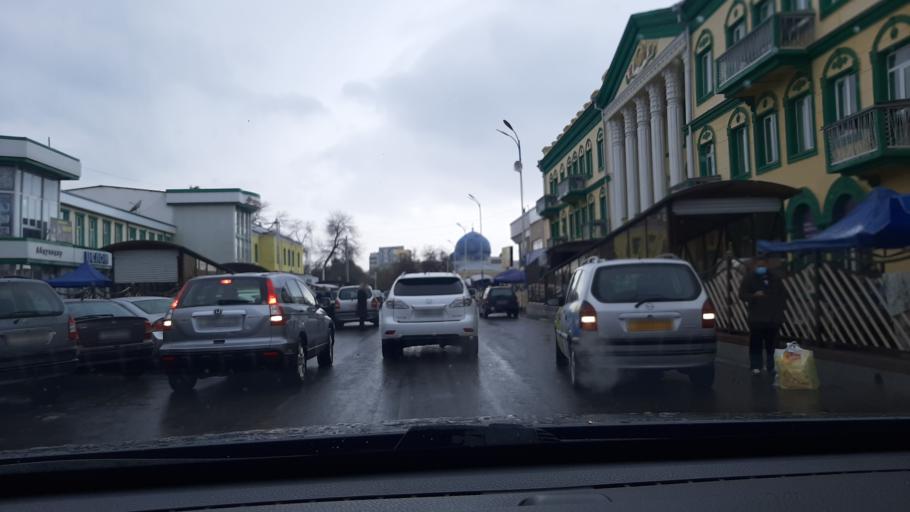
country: TJ
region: Viloyati Sughd
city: Khujand
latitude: 40.2784
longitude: 69.6333
